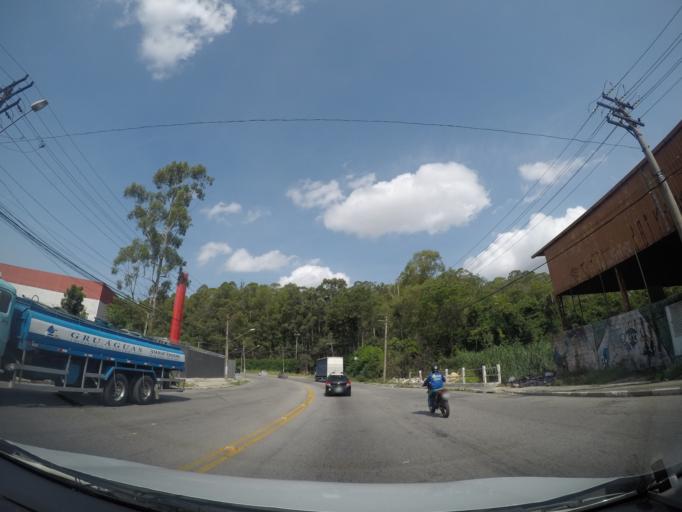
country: BR
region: Sao Paulo
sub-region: Guarulhos
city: Guarulhos
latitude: -23.4372
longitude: -46.4588
